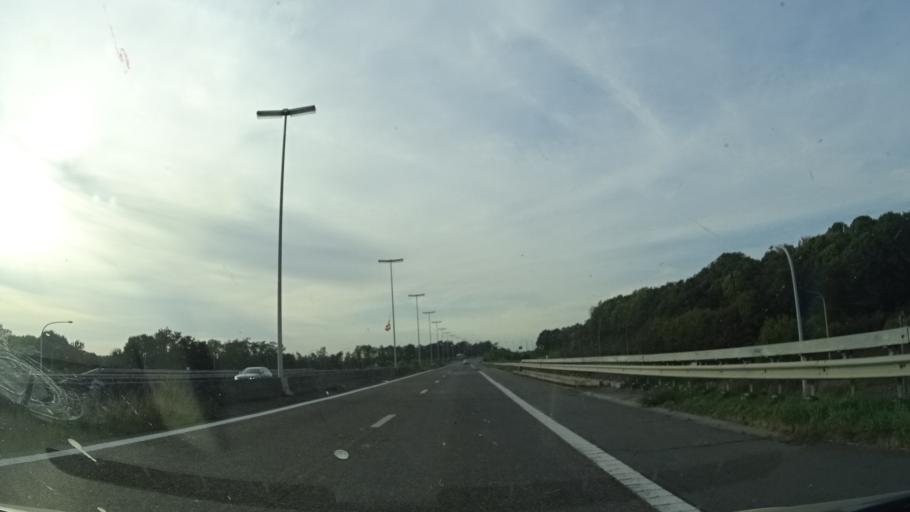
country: BE
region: Wallonia
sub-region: Province du Hainaut
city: Chasse Royale
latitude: 50.4135
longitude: 3.9291
